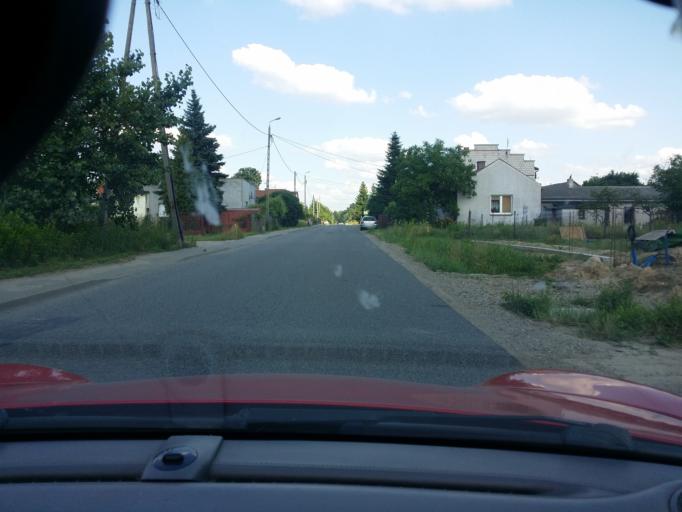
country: PL
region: Masovian Voivodeship
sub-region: Powiat radomski
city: Trablice
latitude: 51.3505
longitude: 21.1475
